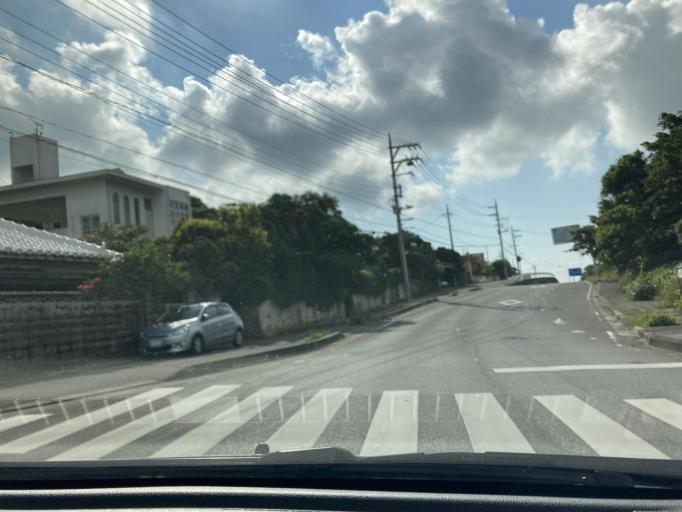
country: JP
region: Okinawa
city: Tomigusuku
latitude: 26.1427
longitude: 127.7681
